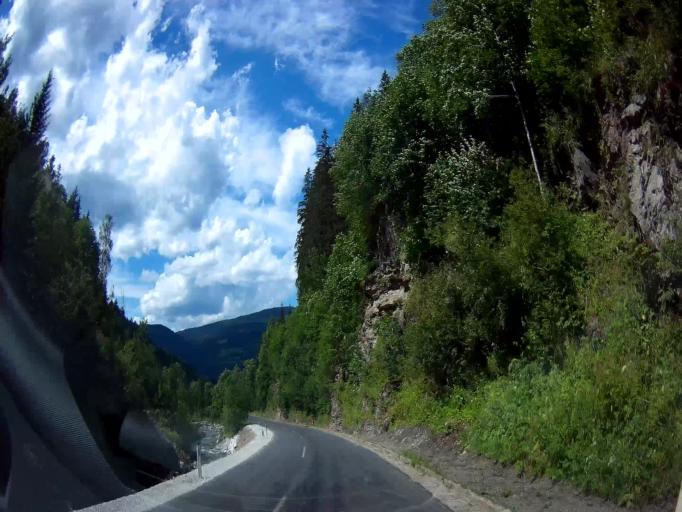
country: AT
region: Styria
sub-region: Politischer Bezirk Murau
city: Stadl an der Mur
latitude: 47.0647
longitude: 13.9874
